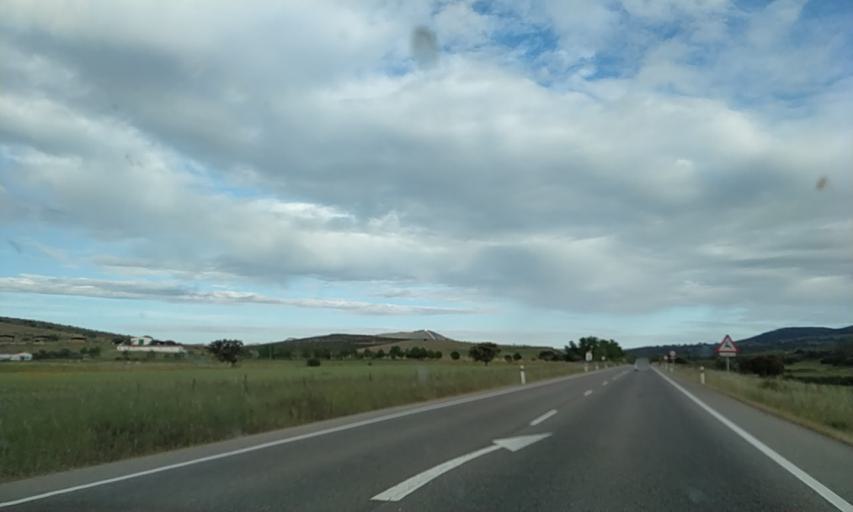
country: ES
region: Extremadura
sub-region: Provincia de Caceres
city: Pedroso de Acim
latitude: 39.8522
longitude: -6.4190
